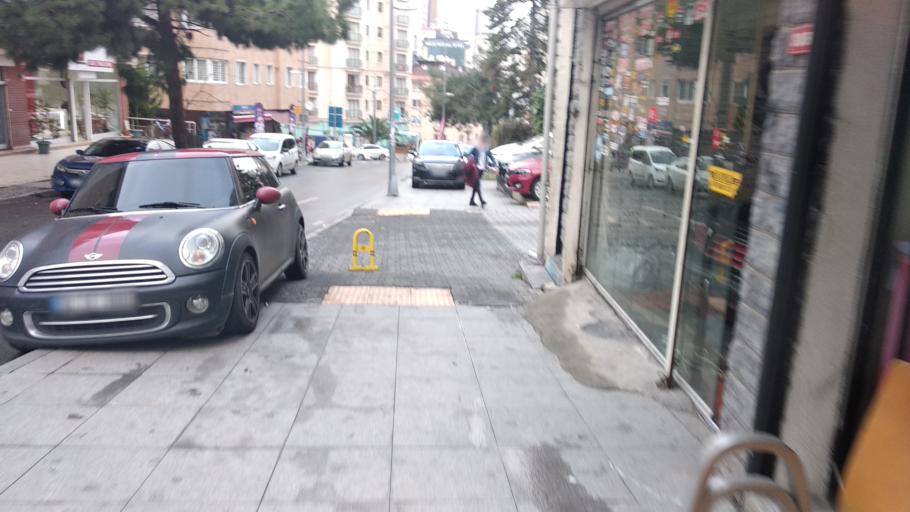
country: TR
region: Istanbul
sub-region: Atasehir
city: Atasehir
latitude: 40.9814
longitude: 29.1128
